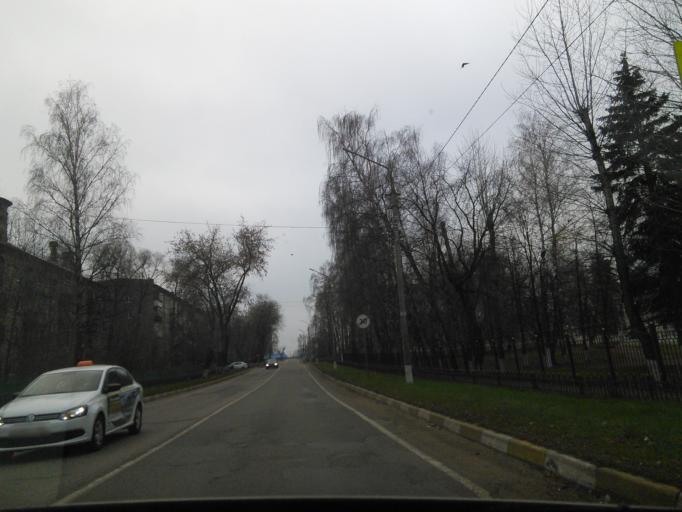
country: RU
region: Moskovskaya
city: Vereya
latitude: 55.6274
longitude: 38.0401
